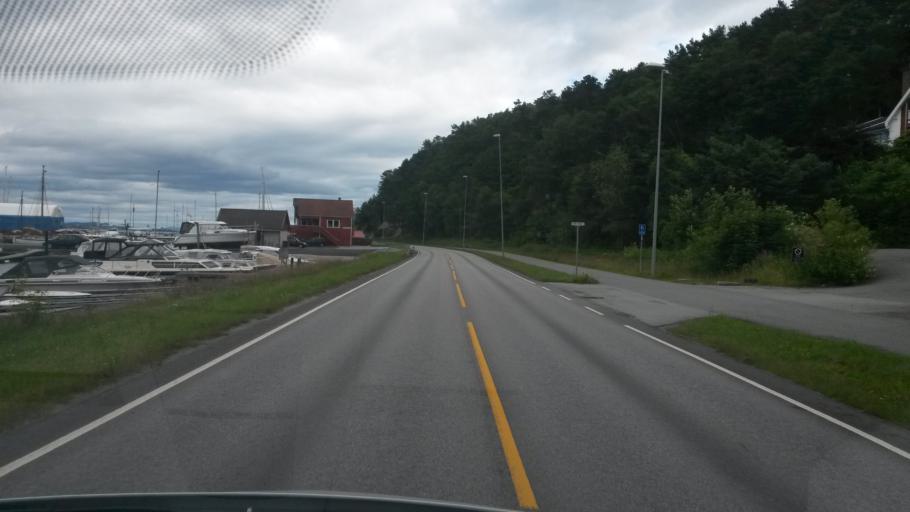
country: NO
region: Rogaland
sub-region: Sandnes
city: Sandnes
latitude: 58.8632
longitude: 5.7550
